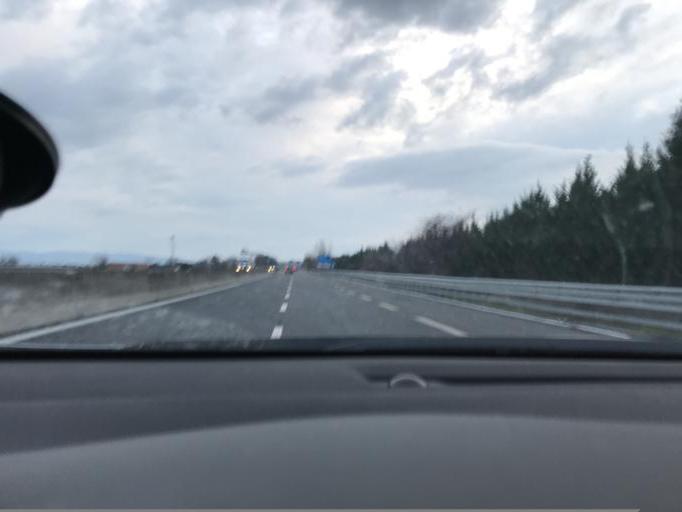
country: IT
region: Umbria
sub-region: Provincia di Perugia
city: Petrignano
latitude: 43.1203
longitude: 12.5128
